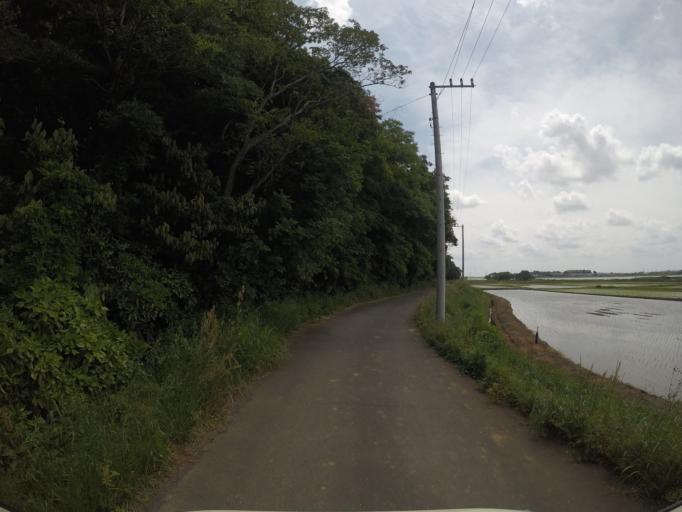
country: JP
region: Ibaraki
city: Ushiku
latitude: 35.9602
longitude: 140.1278
